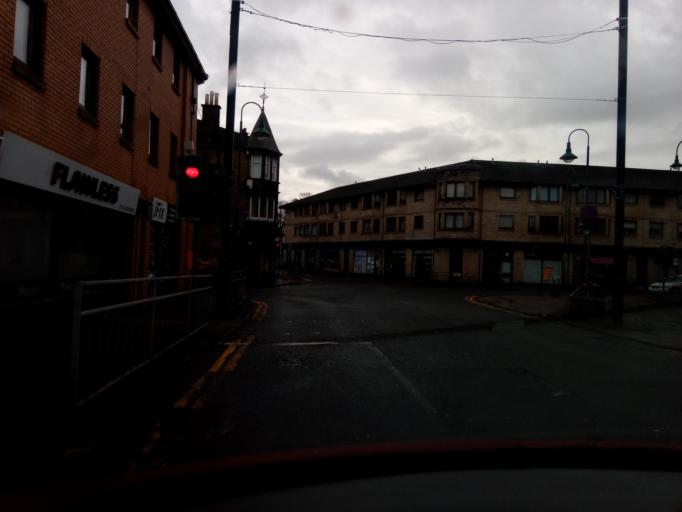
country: GB
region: Scotland
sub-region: East Dunbartonshire
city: Kirkintilloch
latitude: 55.9360
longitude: -4.1523
